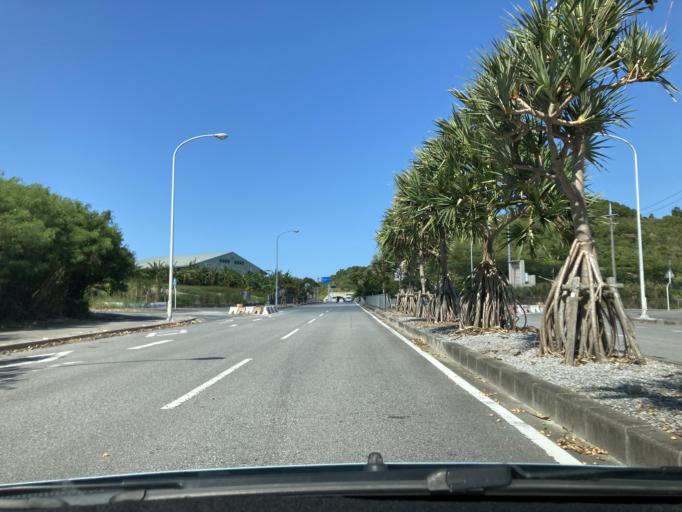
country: JP
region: Okinawa
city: Tomigusuku
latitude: 26.1841
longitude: 127.7221
